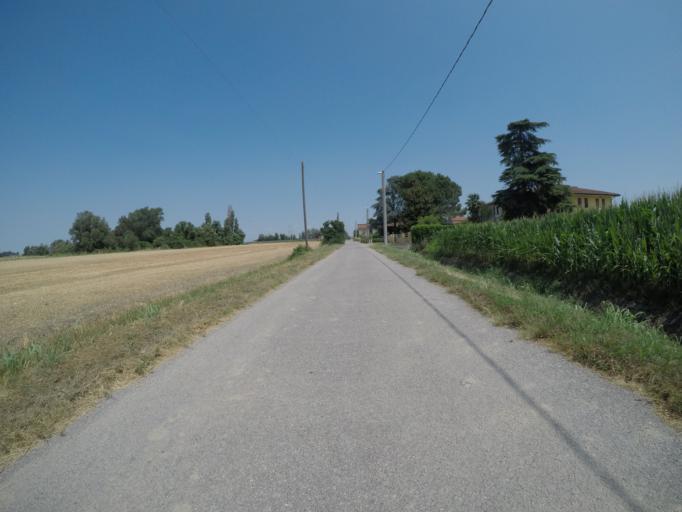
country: IT
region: Veneto
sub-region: Provincia di Rovigo
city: Fratta Polesine
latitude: 45.0188
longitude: 11.6617
